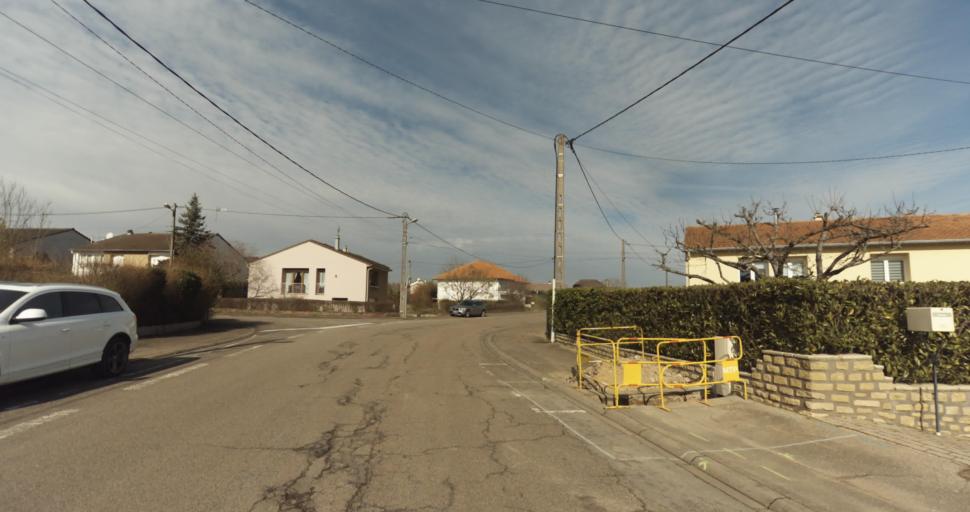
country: FR
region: Lorraine
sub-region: Departement de Meurthe-et-Moselle
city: Jarny
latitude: 49.1548
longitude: 5.8707
